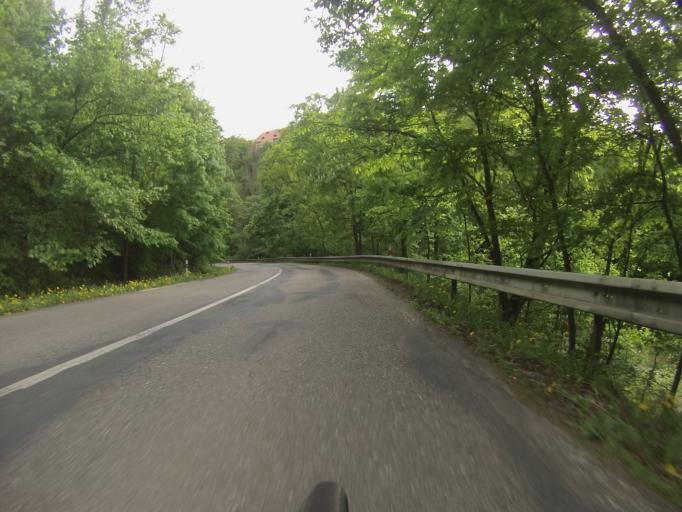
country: CZ
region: South Moravian
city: Veverska Bityska
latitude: 49.2575
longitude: 16.4638
